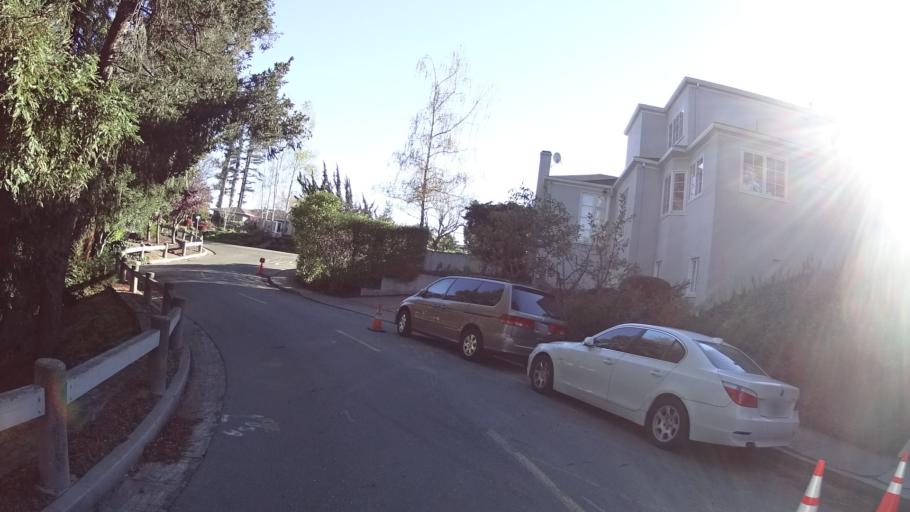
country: US
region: California
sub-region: Alameda County
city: Piedmont
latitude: 37.8273
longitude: -122.2247
